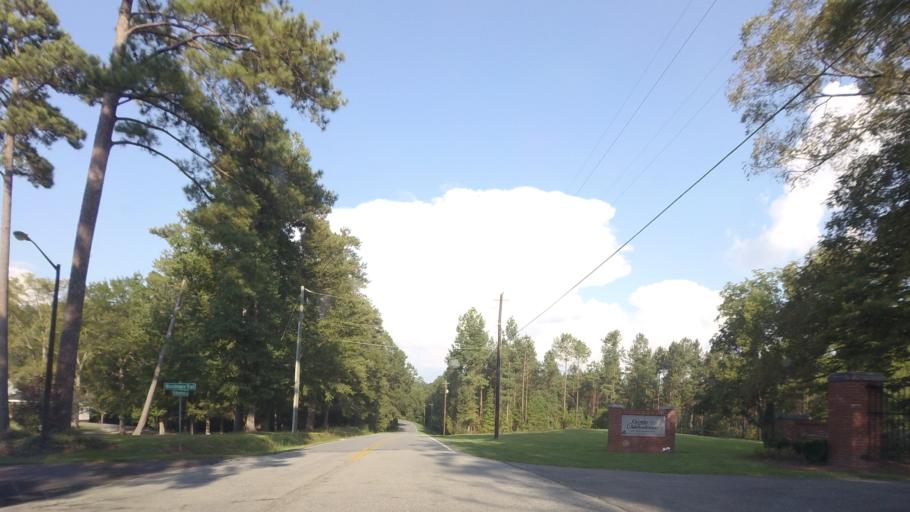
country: US
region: Georgia
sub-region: Bibb County
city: Macon
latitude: 32.8472
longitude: -83.7132
